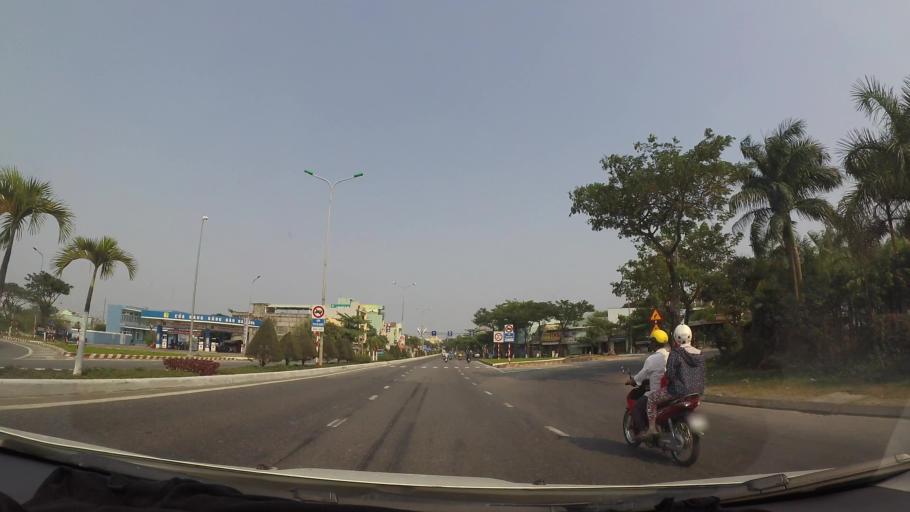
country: VN
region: Da Nang
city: Cam Le
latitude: 16.0141
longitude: 108.1954
